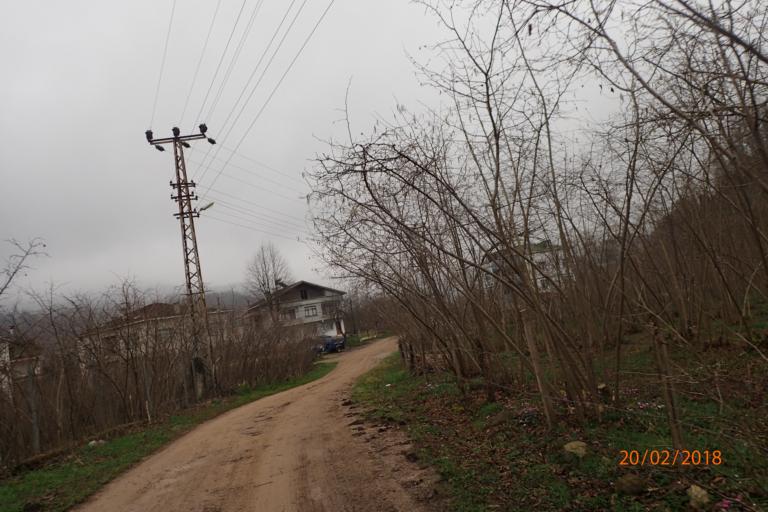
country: TR
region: Ordu
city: Camas
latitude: 40.9474
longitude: 37.5327
